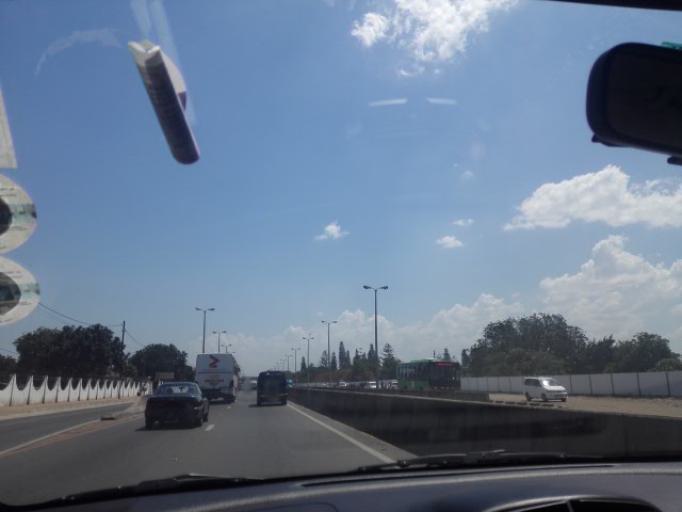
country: MZ
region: Maputo City
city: Maputo
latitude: -25.9369
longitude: 32.5483
